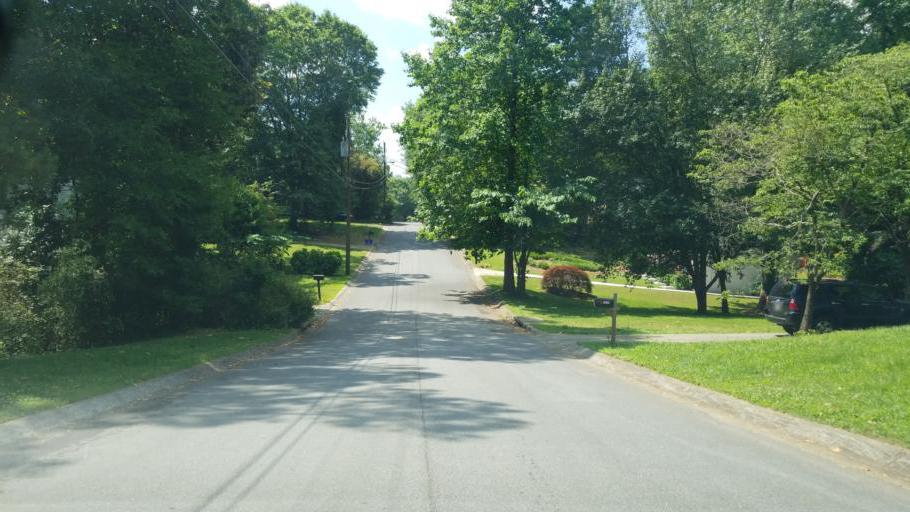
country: US
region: Georgia
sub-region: Cobb County
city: Smyrna
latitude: 33.8887
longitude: -84.4851
